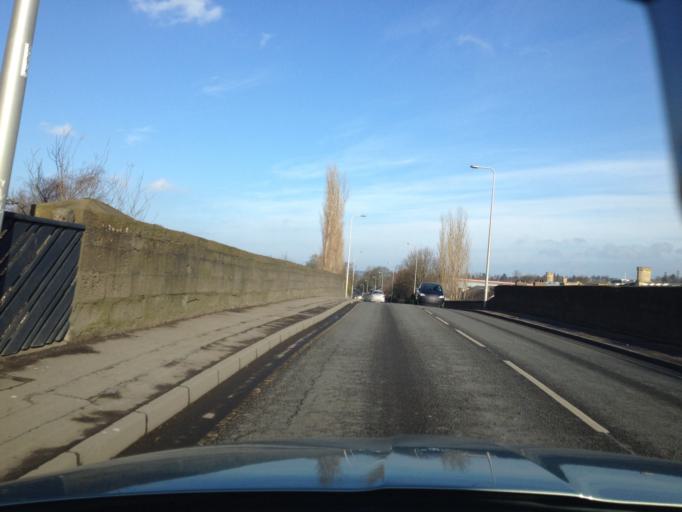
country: GB
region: Scotland
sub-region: Perth and Kinross
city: Perth
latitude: 56.3832
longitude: -3.4339
